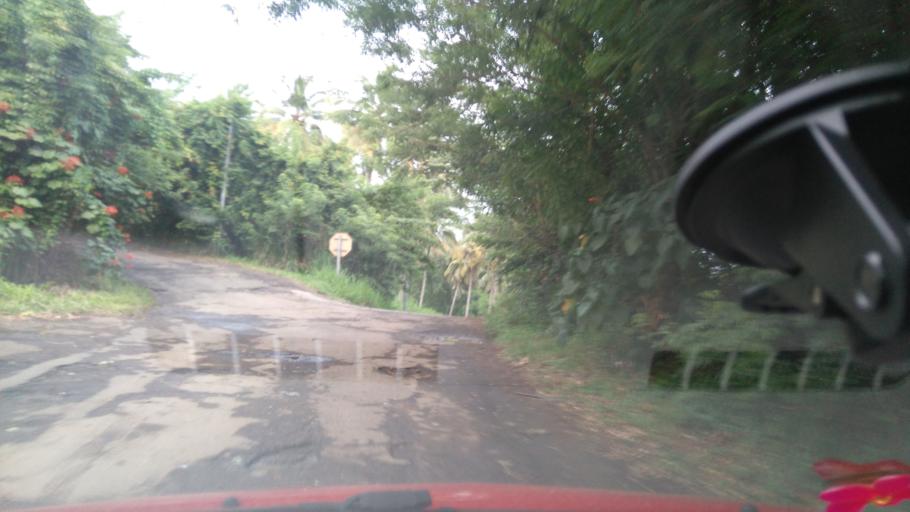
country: MQ
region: Martinique
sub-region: Martinique
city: Ducos
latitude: 14.5537
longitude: -60.9691
